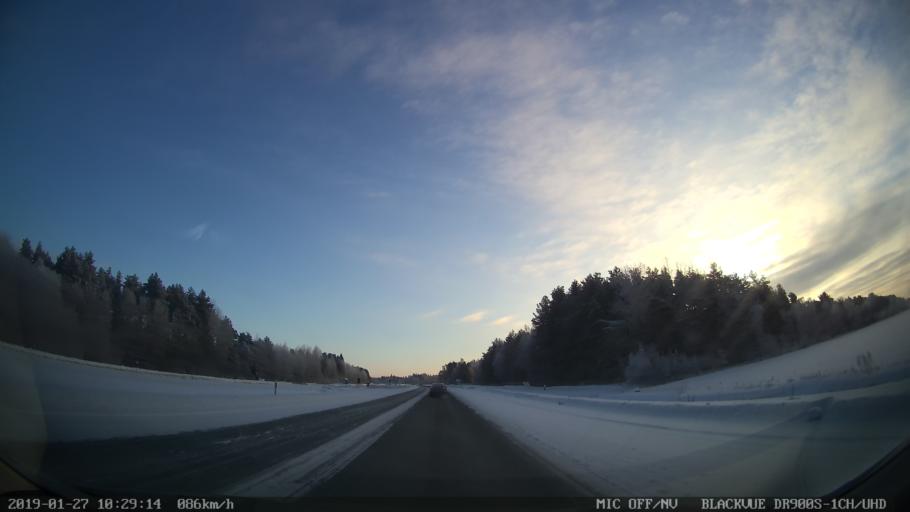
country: EE
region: Harju
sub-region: Raasiku vald
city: Raasiku
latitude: 59.4360
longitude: 25.1626
